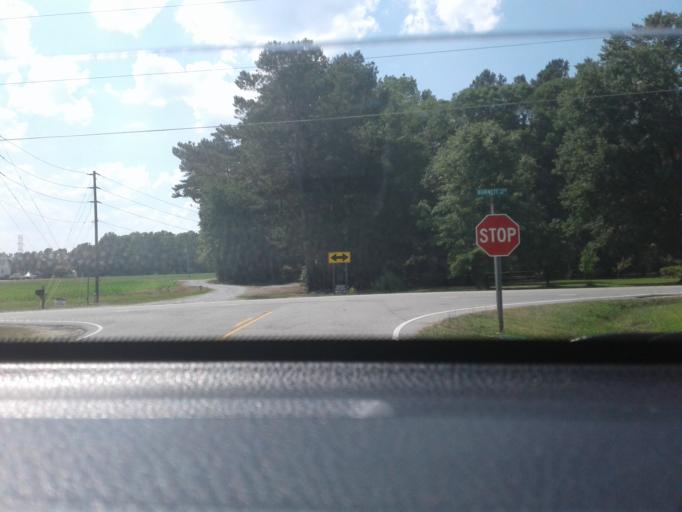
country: US
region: North Carolina
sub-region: Harnett County
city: Erwin
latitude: 35.2216
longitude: -78.6883
